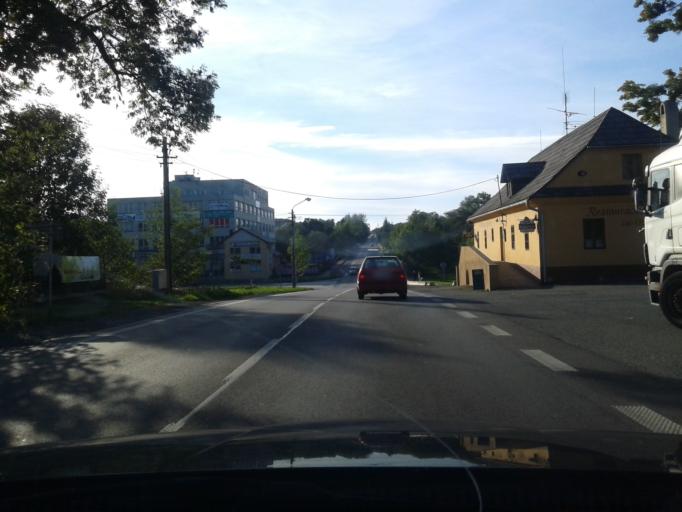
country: CZ
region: Moravskoslezsky
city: Trinec
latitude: 49.6625
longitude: 18.6533
